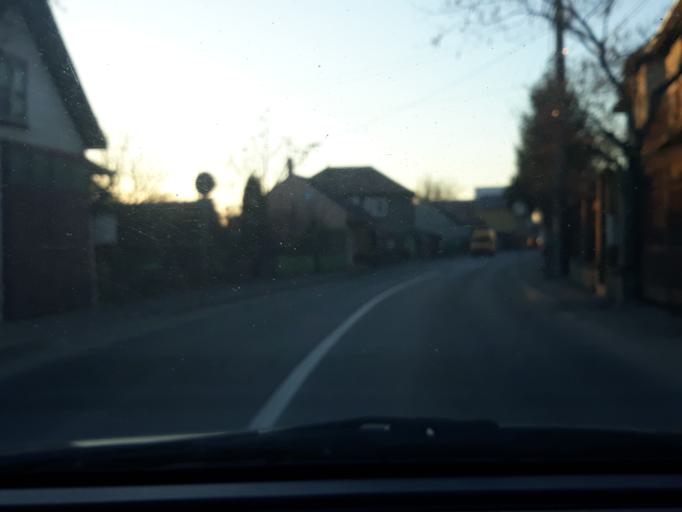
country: RO
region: Bihor
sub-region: Comuna Biharea
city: Oradea
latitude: 47.0524
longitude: 21.9582
